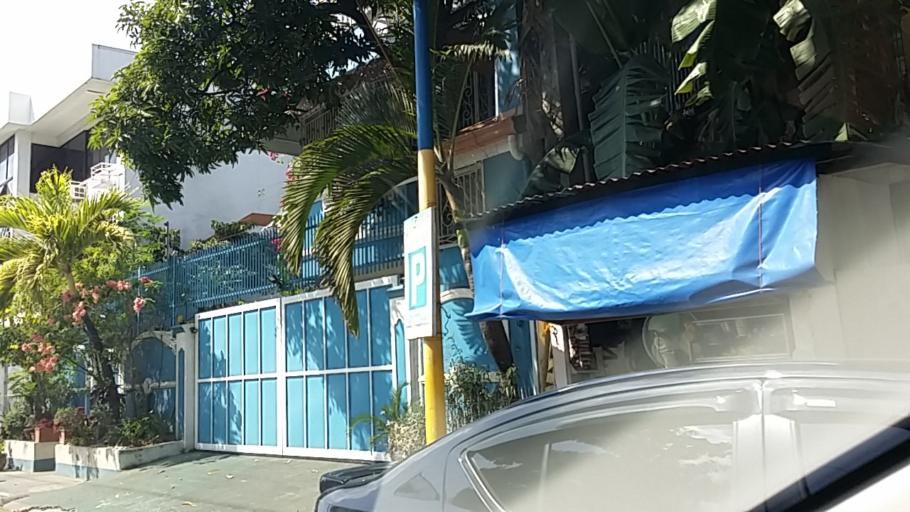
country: PH
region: Metro Manila
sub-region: Mandaluyong
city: Mandaluyong City
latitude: 14.5718
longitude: 121.0347
